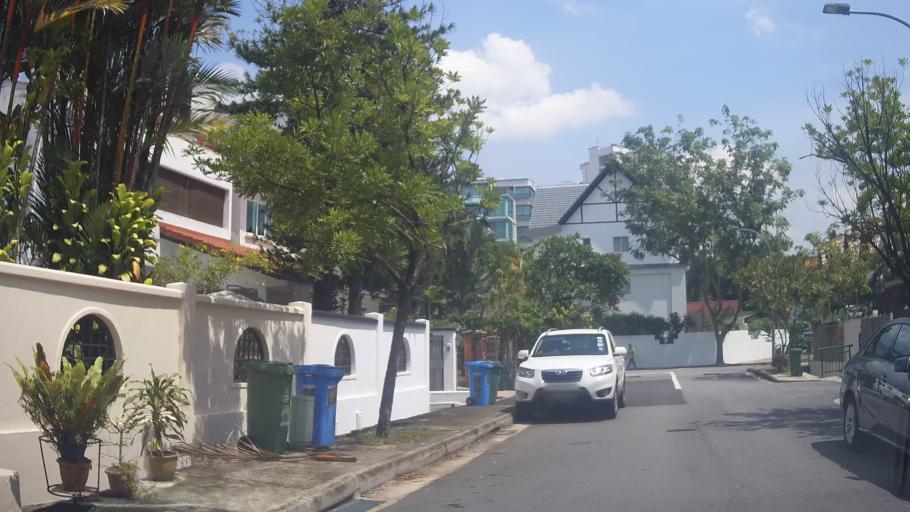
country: SG
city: Singapore
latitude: 1.3235
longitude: 103.8022
